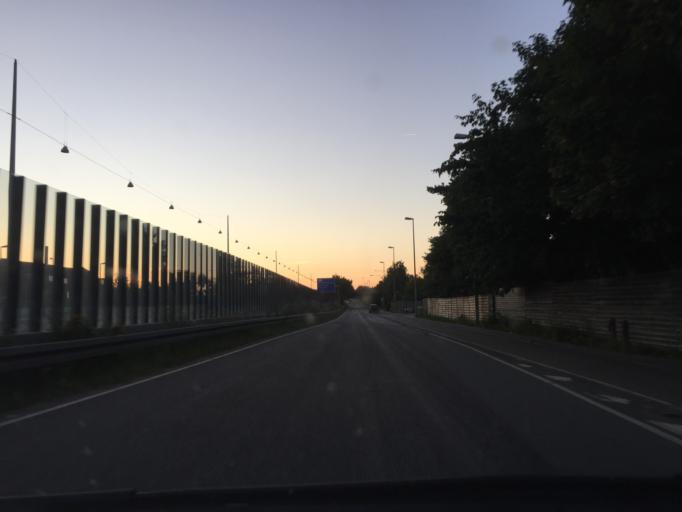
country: DK
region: Capital Region
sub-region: Lyngby-Tarbaek Kommune
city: Kongens Lyngby
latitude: 55.7412
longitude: 12.5363
